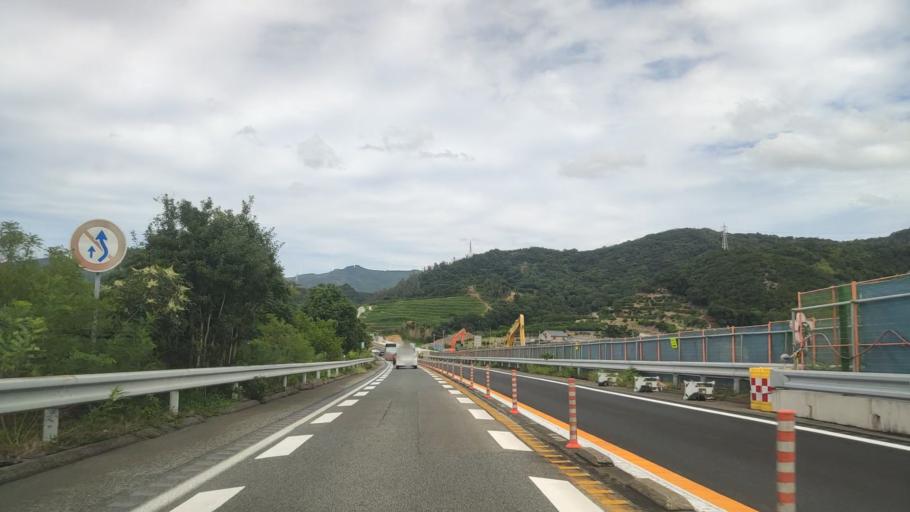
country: JP
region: Wakayama
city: Gobo
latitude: 33.9124
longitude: 135.1944
